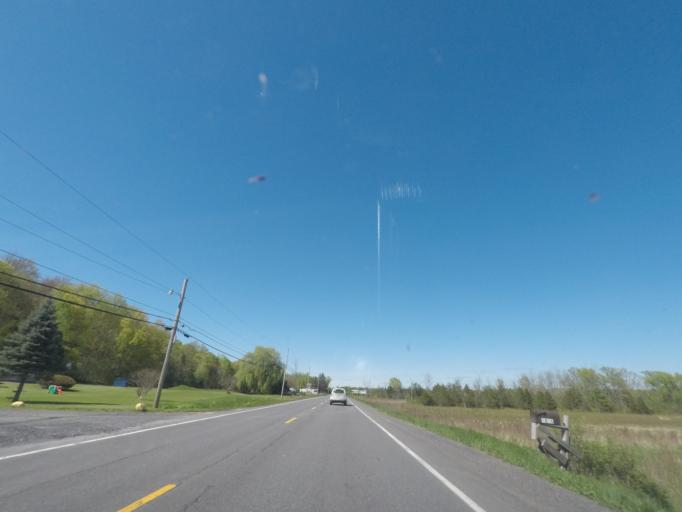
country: US
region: New York
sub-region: Greene County
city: Jefferson Heights
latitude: 42.2742
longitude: -73.8575
